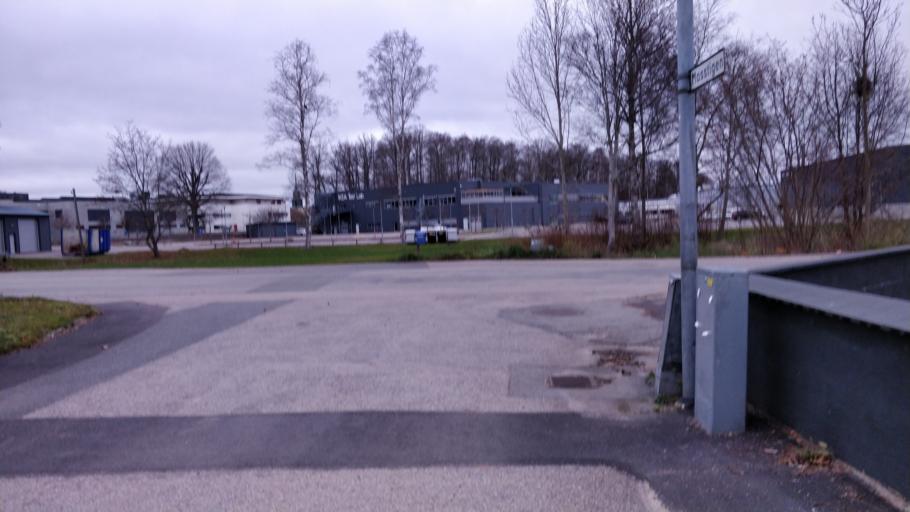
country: SE
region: Kronoberg
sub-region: Almhults Kommun
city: AElmhult
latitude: 56.5476
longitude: 14.1307
